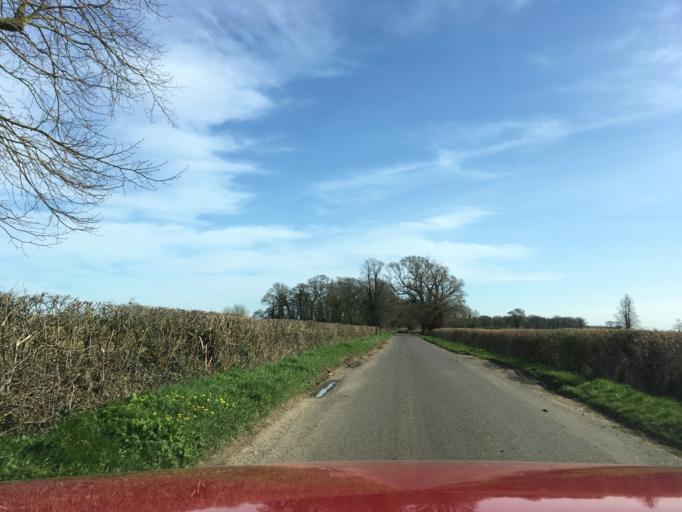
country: GB
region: England
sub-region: Wiltshire
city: Luckington
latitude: 51.5456
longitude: -2.2261
